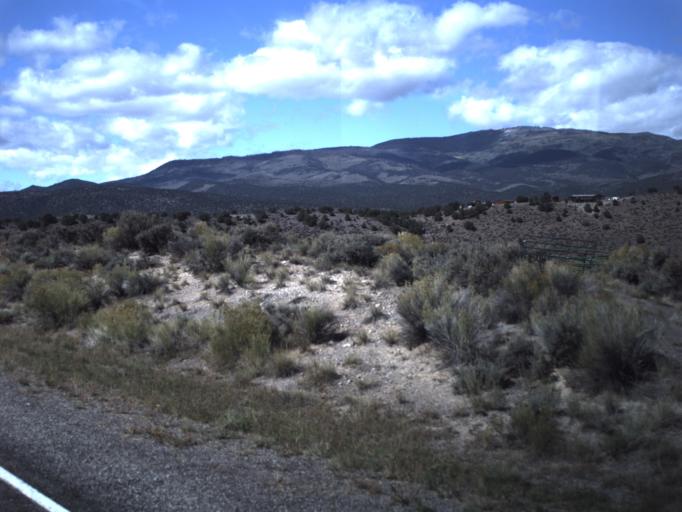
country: US
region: Utah
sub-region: Wayne County
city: Loa
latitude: 38.5672
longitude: -111.8429
